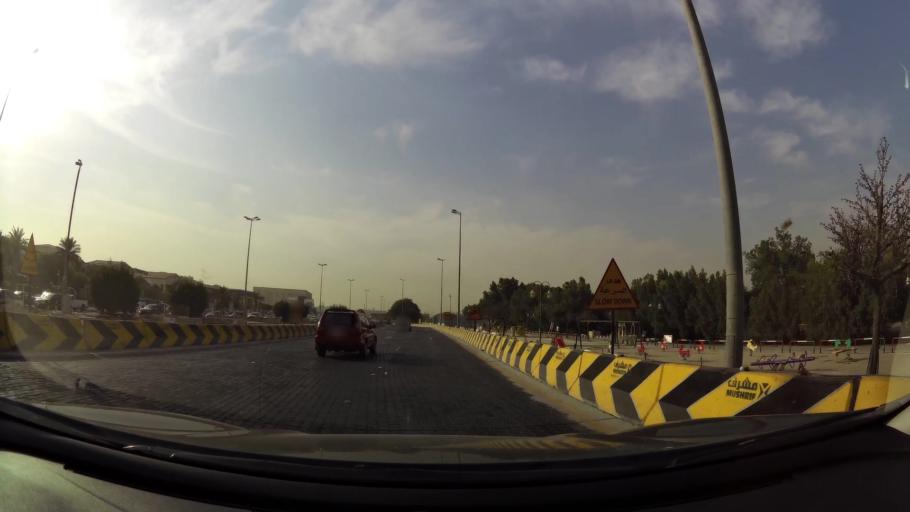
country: KW
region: Muhafazat Hawalli
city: Ar Rumaythiyah
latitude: 29.3207
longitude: 48.0876
